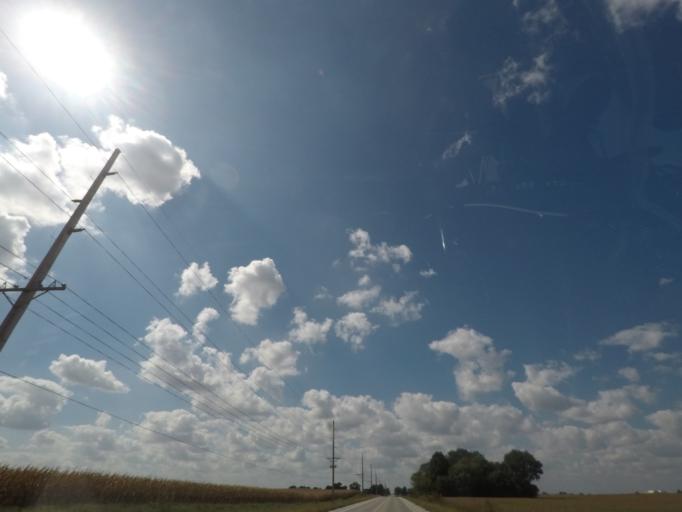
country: US
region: Iowa
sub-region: Story County
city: Nevada
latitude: 42.0231
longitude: -93.5320
